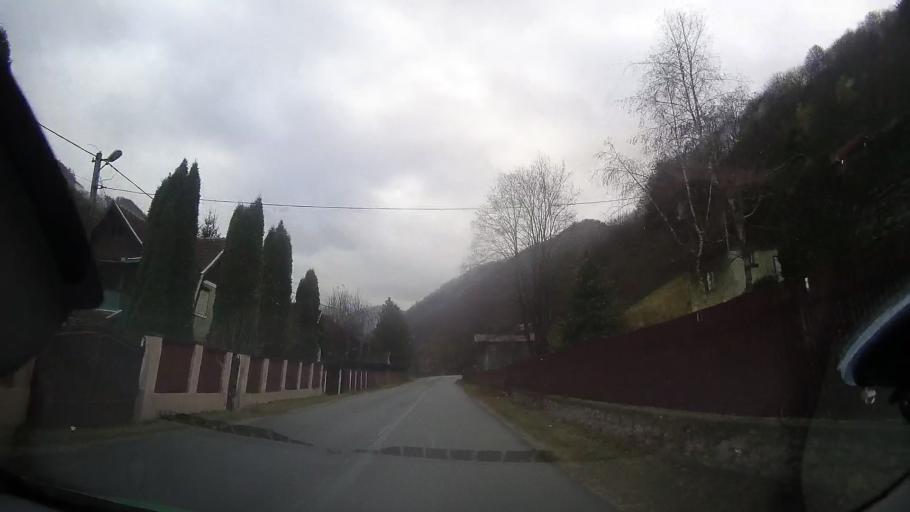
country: RO
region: Cluj
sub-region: Comuna Maguri-Racatau
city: Maguri-Racatau
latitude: 46.6528
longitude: 23.2016
